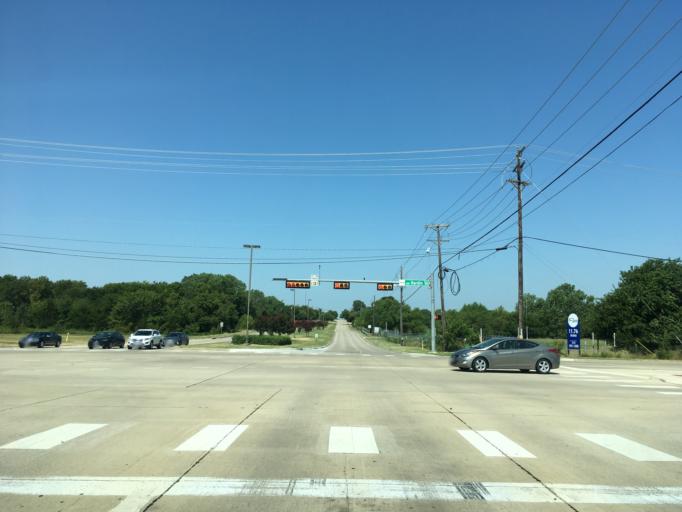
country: US
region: Texas
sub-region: Collin County
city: Fairview
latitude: 33.1591
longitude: -96.6630
